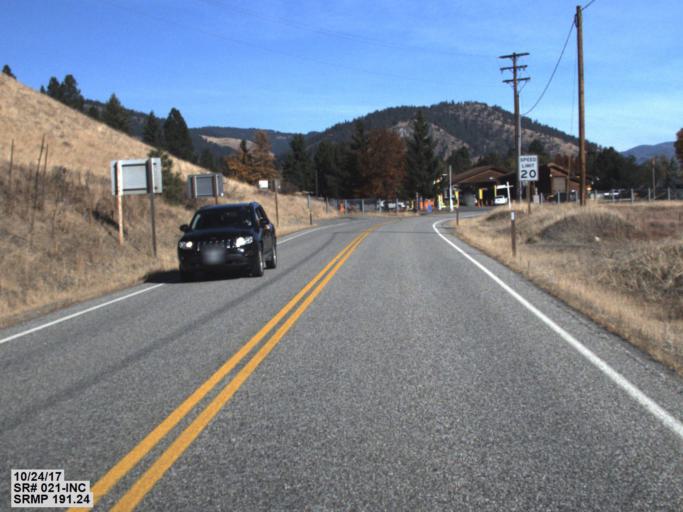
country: CA
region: British Columbia
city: Grand Forks
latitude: 48.9986
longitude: -118.5043
